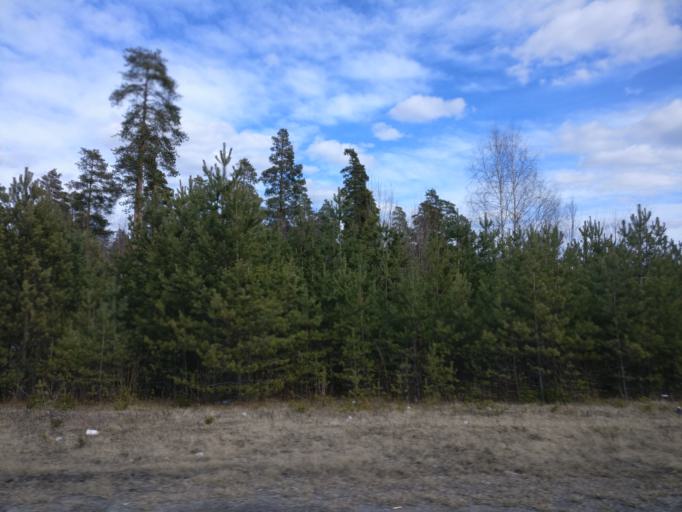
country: FI
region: Pirkanmaa
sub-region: Etelae-Pirkanmaa
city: Viiala
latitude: 61.2558
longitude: 23.8372
